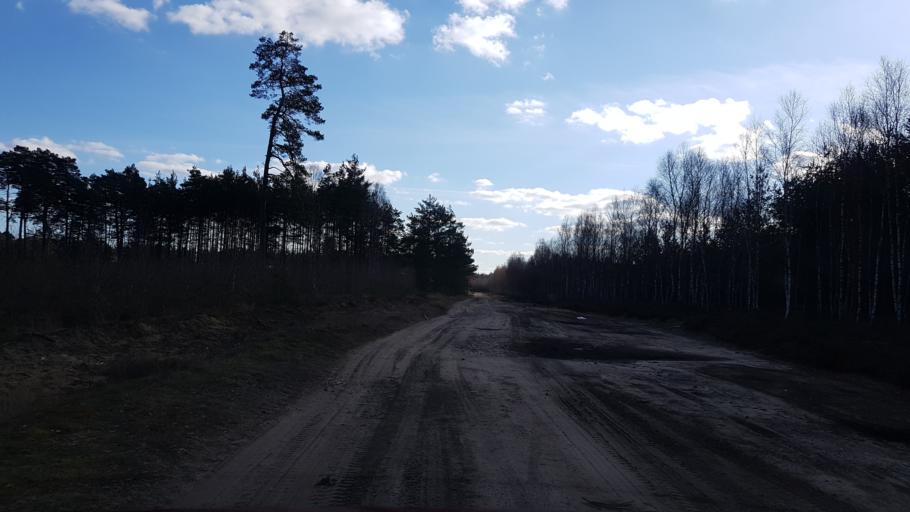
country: PL
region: Greater Poland Voivodeship
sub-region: Powiat zlotowski
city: Sypniewo
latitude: 53.5377
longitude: 16.6466
